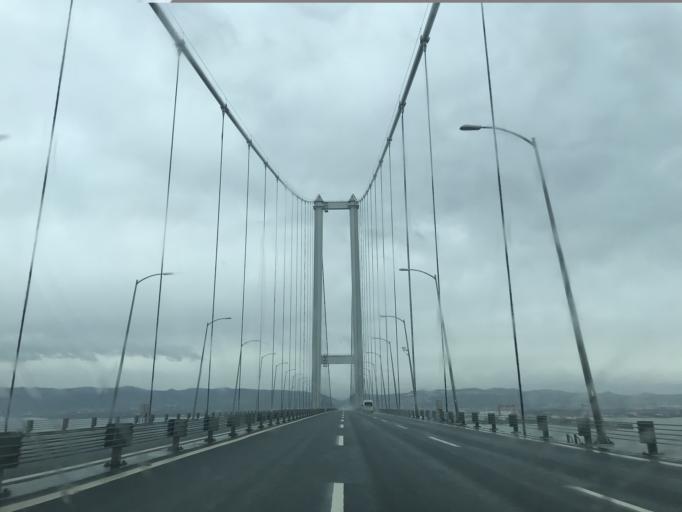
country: TR
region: Yalova
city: Altinova
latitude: 40.7524
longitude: 29.5153
